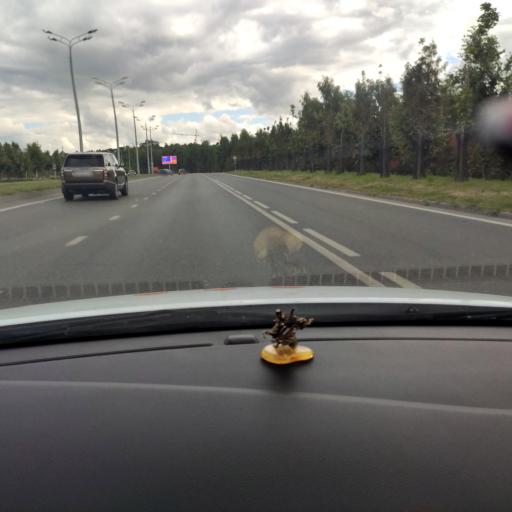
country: RU
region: Tatarstan
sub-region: Gorod Kazan'
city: Kazan
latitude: 55.7415
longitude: 49.1759
